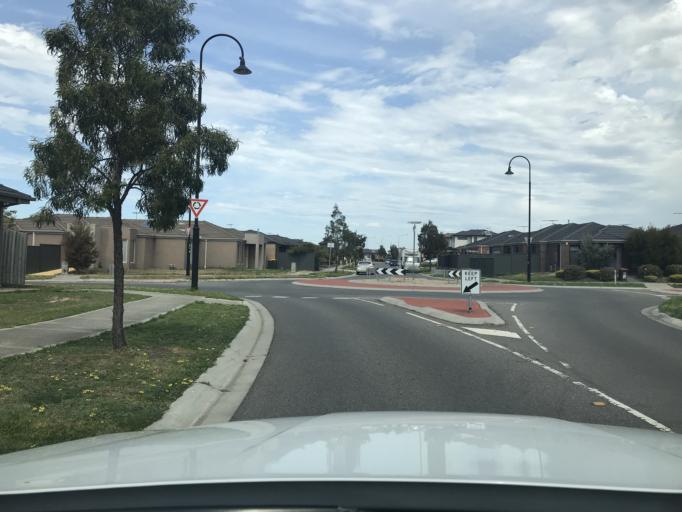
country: AU
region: Victoria
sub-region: Hume
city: Roxburgh Park
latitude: -37.6037
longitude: 144.9118
